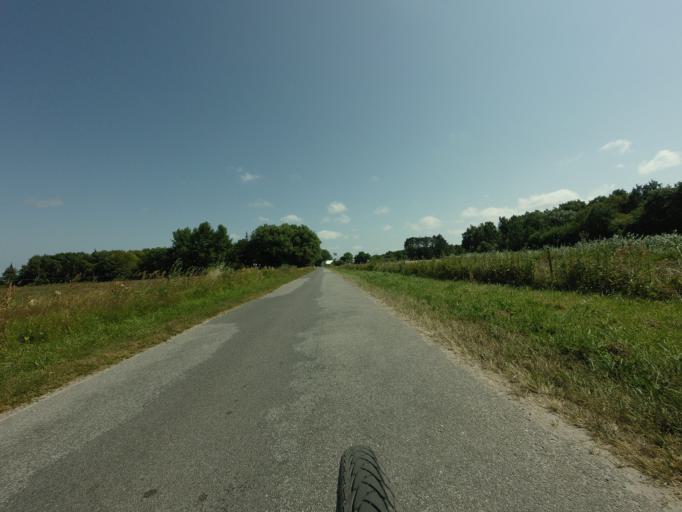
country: DK
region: North Denmark
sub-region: Laeso Kommune
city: Byrum
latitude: 57.2514
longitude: 10.9852
